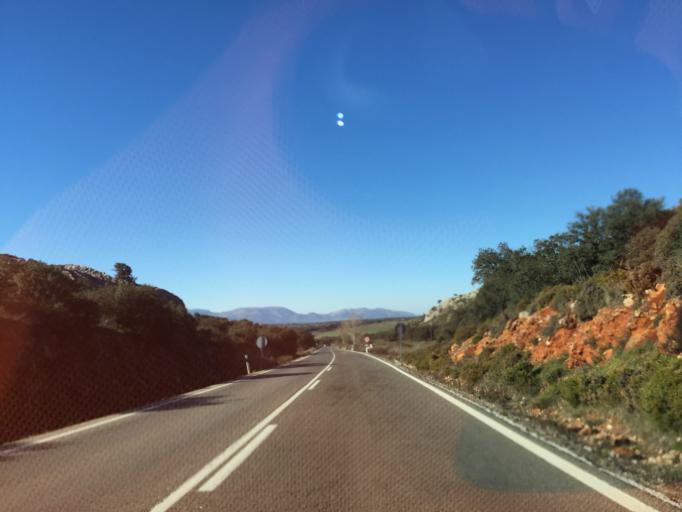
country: ES
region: Andalusia
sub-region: Provincia de Malaga
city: Cuevas del Becerro
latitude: 36.8463
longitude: -5.0571
